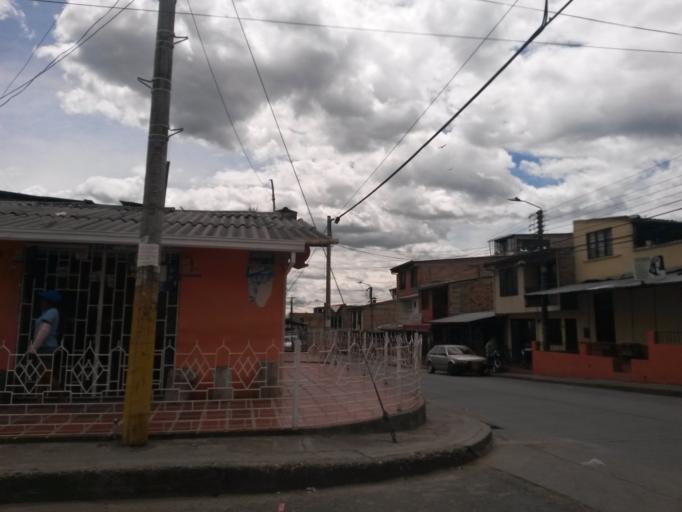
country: CO
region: Cauca
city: Popayan
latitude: 2.4543
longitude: -76.6313
